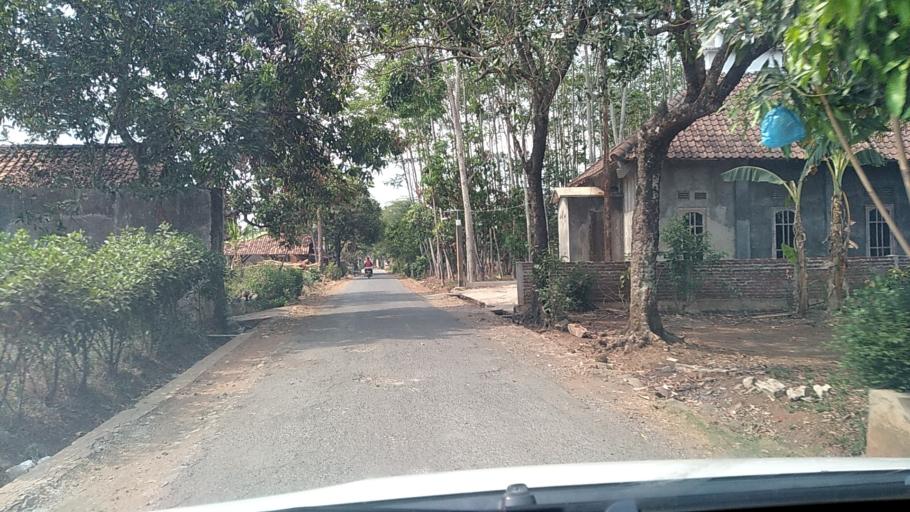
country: ID
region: Central Java
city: Ungaran
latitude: -7.0642
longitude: 110.3050
